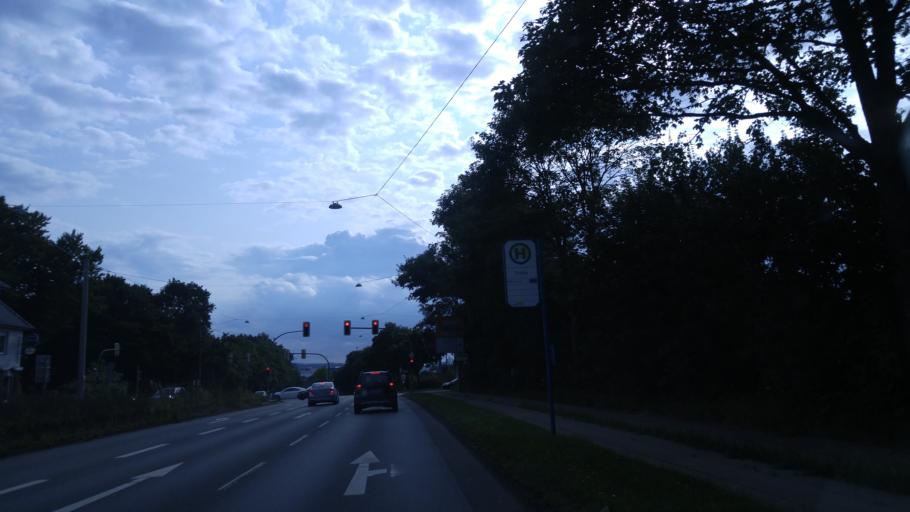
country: DE
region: North Rhine-Westphalia
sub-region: Regierungsbezirk Detmold
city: Bielefeld
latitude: 52.0499
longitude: 8.5866
